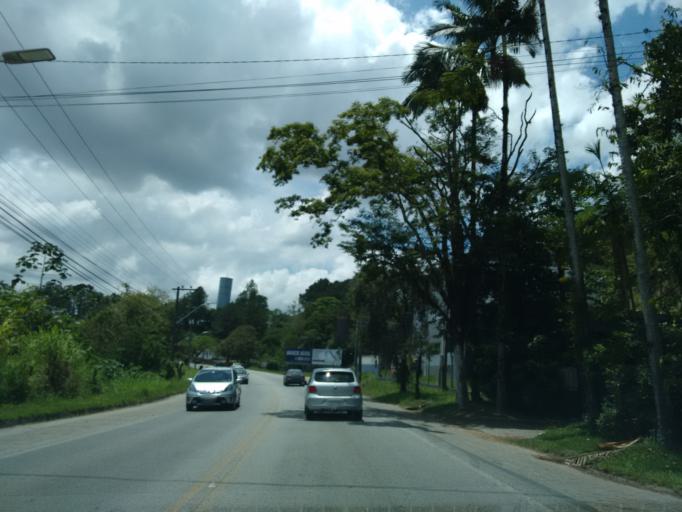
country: BR
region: Santa Catarina
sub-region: Blumenau
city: Blumenau
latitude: -26.9051
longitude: -49.0158
